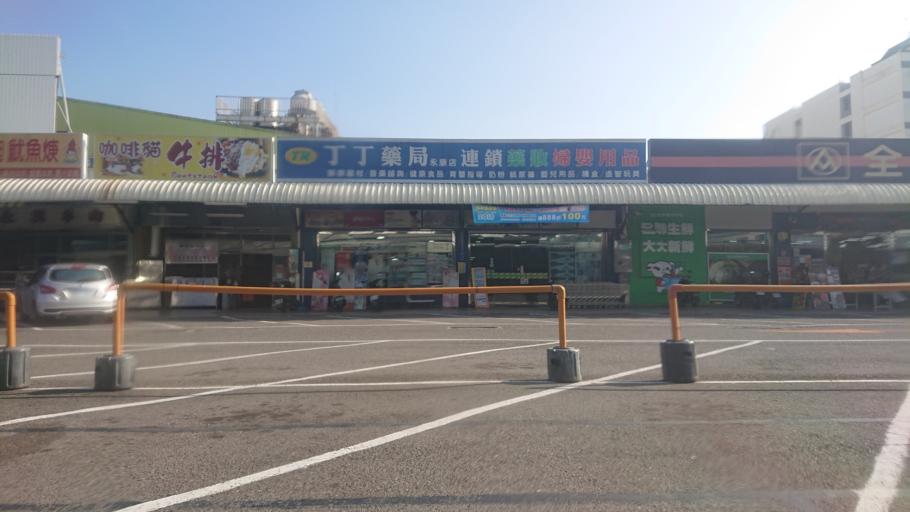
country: TW
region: Taiwan
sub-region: Tainan
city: Tainan
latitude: 23.0145
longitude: 120.2351
